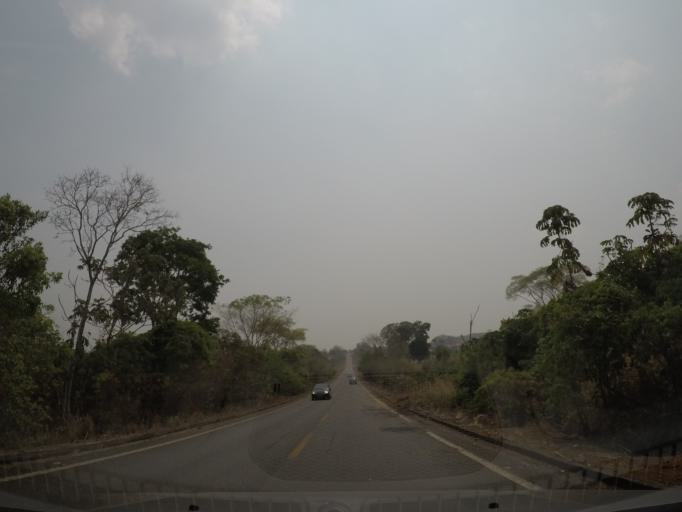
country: BR
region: Goias
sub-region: Pirenopolis
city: Pirenopolis
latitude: -15.8978
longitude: -48.8749
